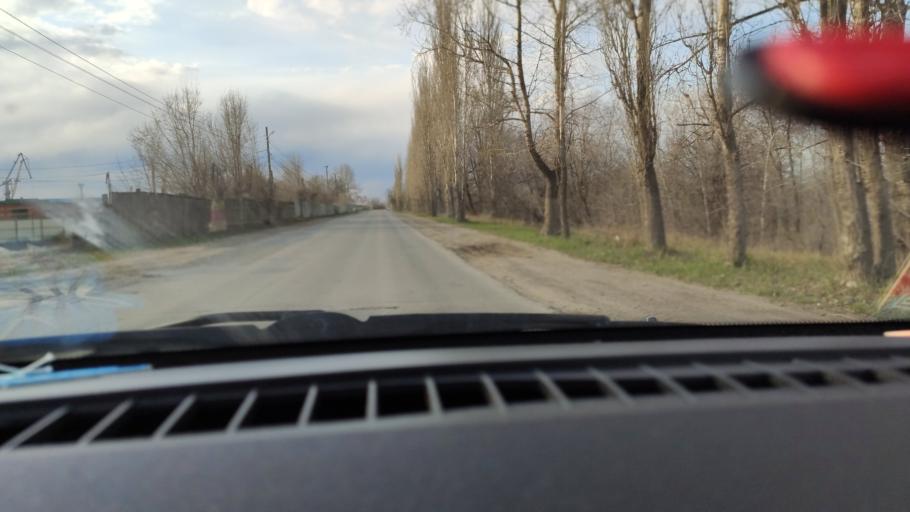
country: RU
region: Saratov
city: Engel's
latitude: 51.4872
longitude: 46.0527
